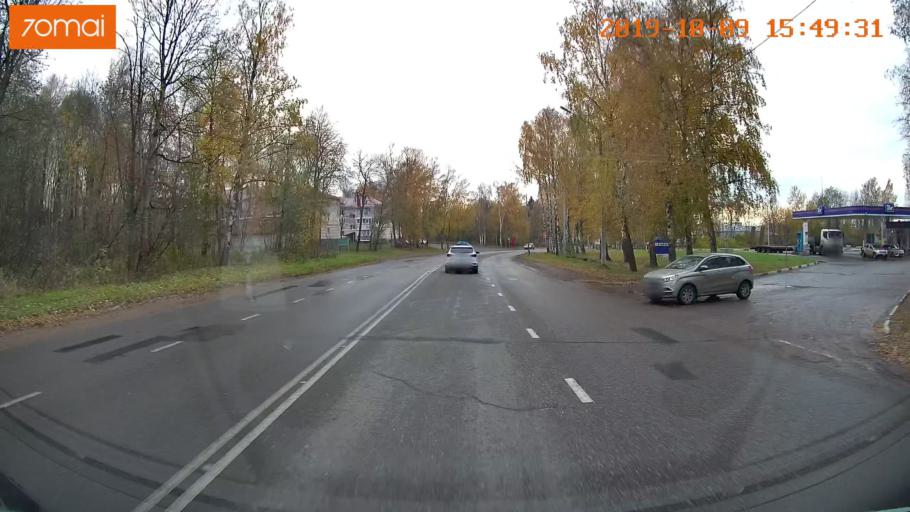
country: RU
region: Kostroma
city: Oktyabr'skiy
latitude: 57.8046
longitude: 41.0039
